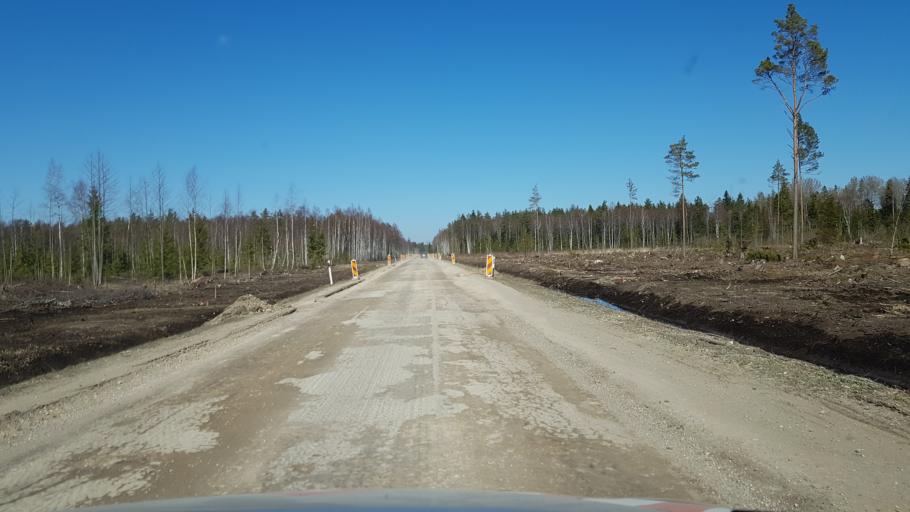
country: EE
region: Laeaene-Virumaa
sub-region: Vinni vald
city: Vinni
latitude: 59.0481
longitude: 26.6580
